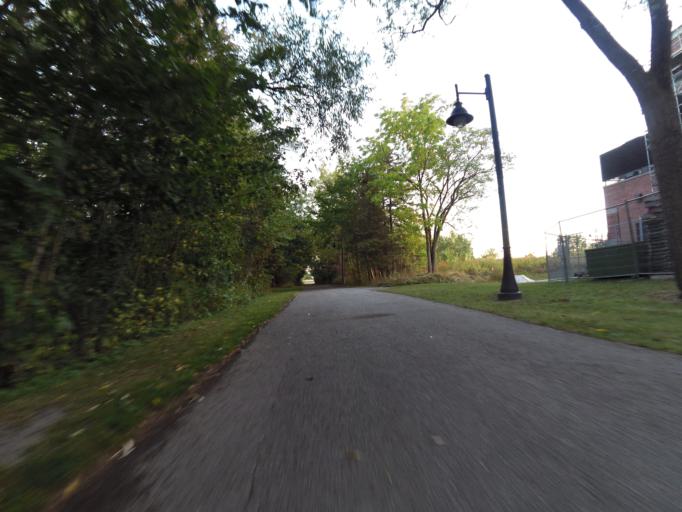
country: CA
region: Ontario
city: Etobicoke
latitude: 43.5936
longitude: -79.5151
